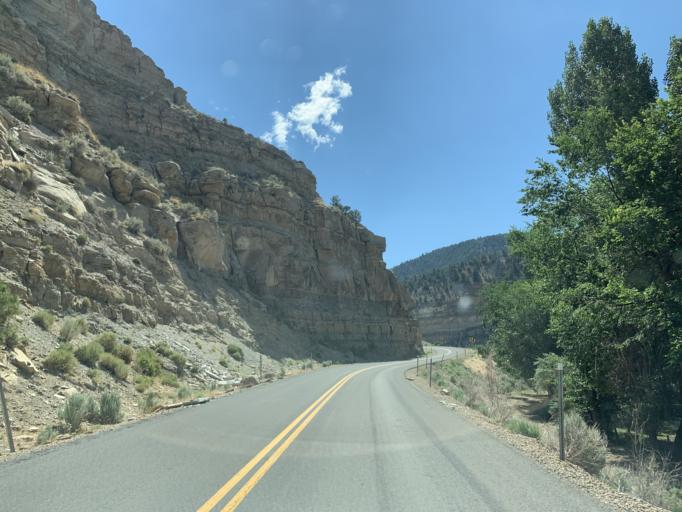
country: US
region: Utah
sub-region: Carbon County
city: East Carbon City
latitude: 39.7787
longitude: -110.4454
